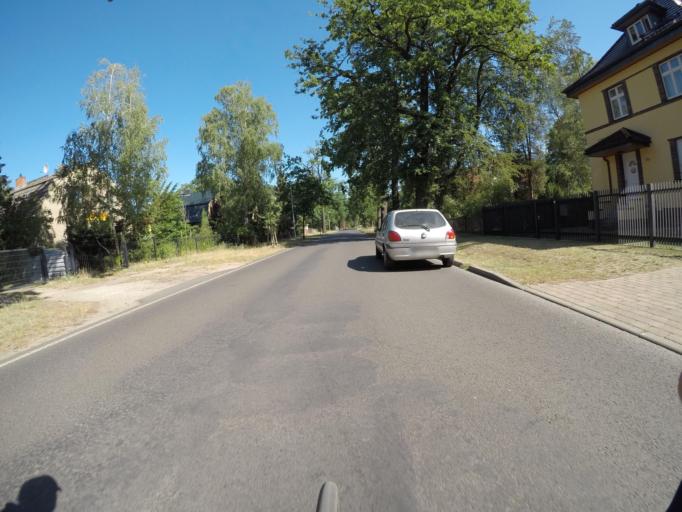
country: DE
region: Brandenburg
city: Schoneiche
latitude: 52.4736
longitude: 13.6937
